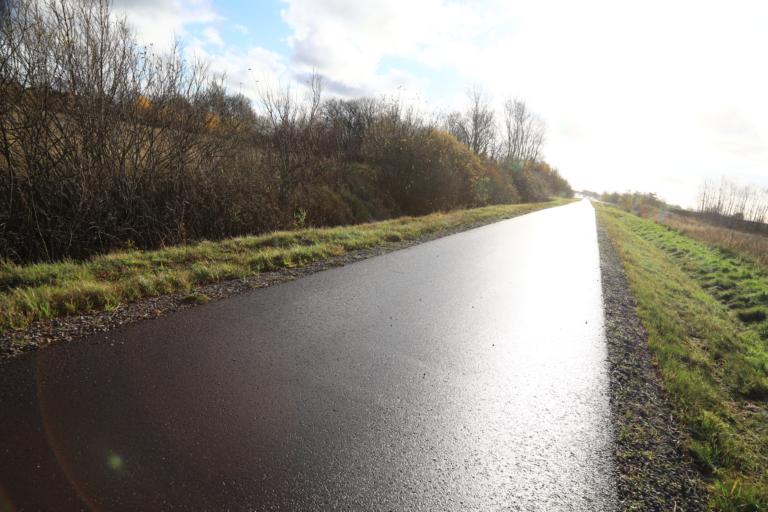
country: SE
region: Halland
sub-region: Varbergs Kommun
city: Traslovslage
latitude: 57.0884
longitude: 12.2869
